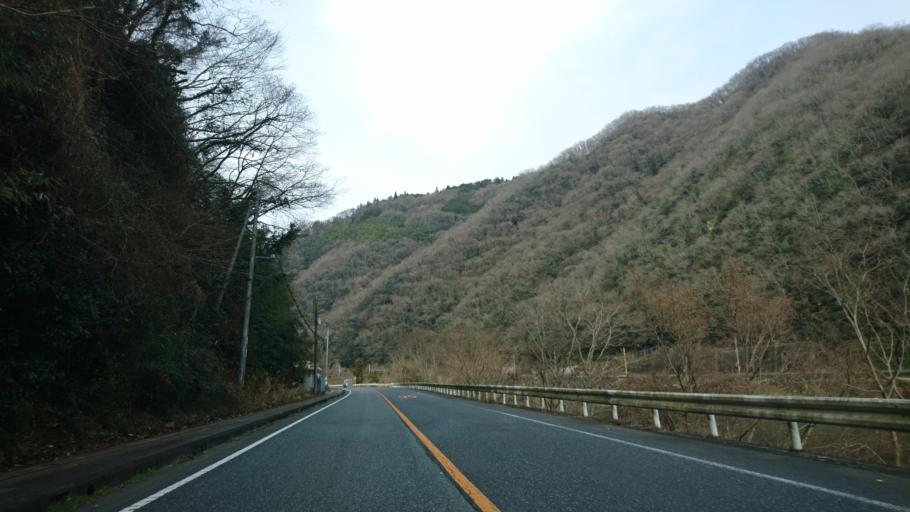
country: JP
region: Okayama
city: Takahashi
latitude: 34.8737
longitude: 133.5620
